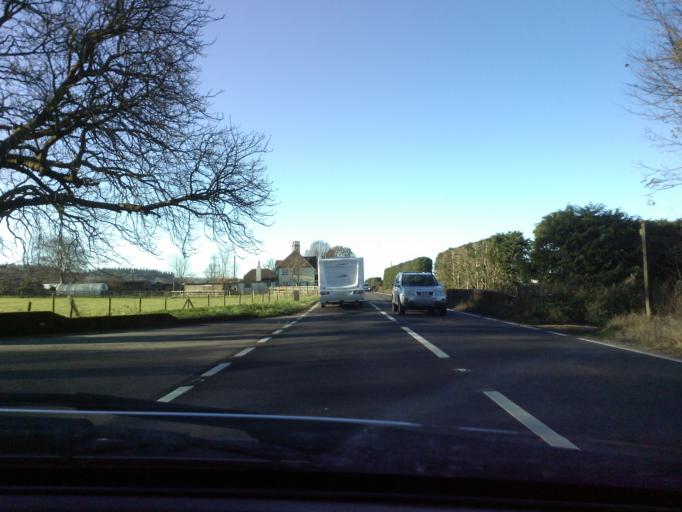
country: GB
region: England
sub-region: Dorset
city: Lytchett Matravers
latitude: 50.7866
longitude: -2.0554
